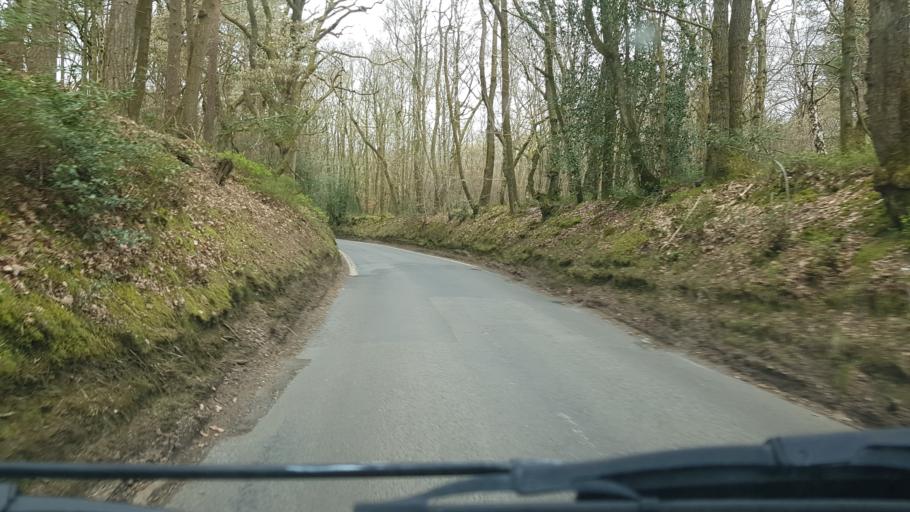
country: GB
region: England
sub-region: Surrey
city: Cranleigh
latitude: 51.1825
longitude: -0.4614
